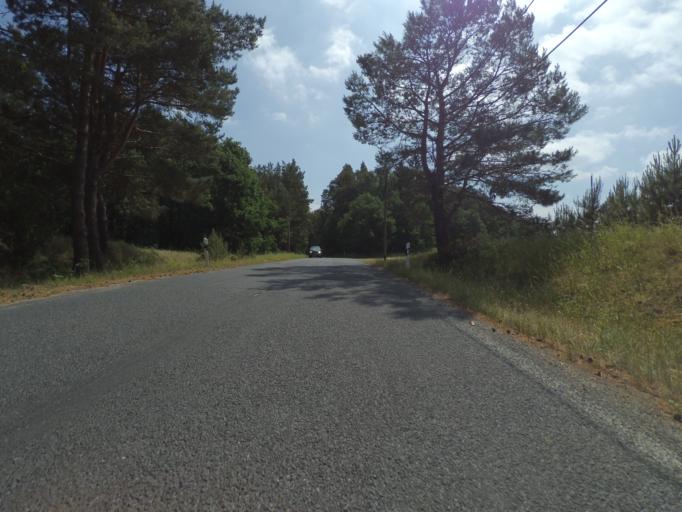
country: DE
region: Mecklenburg-Vorpommern
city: Plau am See
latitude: 53.4239
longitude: 12.3234
